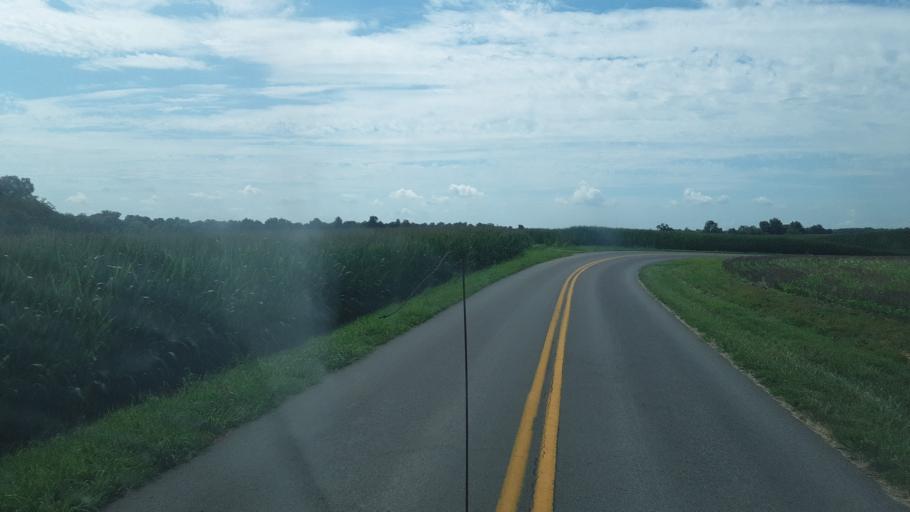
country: US
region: Kentucky
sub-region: Christian County
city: Oak Grove
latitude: 36.7459
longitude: -87.3170
